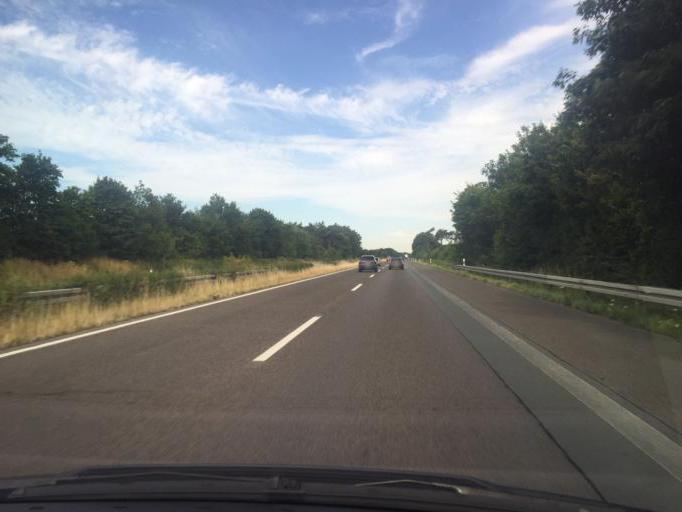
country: DE
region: North Rhine-Westphalia
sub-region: Regierungsbezirk Dusseldorf
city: Sonsbeck
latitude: 51.5806
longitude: 6.4051
